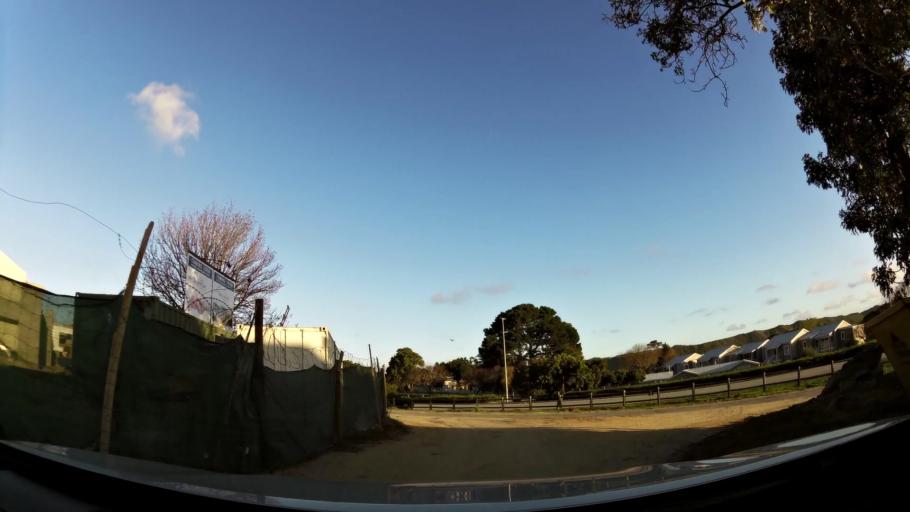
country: ZA
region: Western Cape
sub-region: Eden District Municipality
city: Knysna
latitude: -34.0118
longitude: 22.7974
